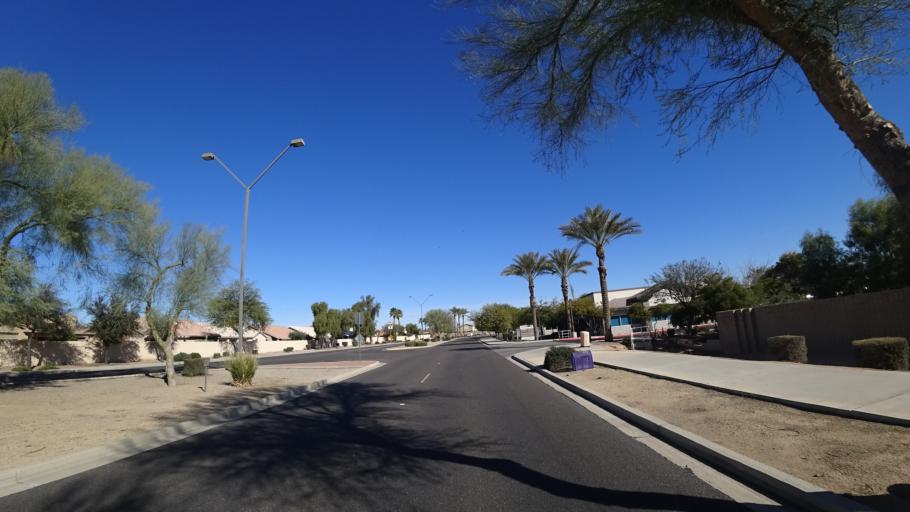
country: US
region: Arizona
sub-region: Maricopa County
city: Litchfield Park
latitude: 33.4848
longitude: -112.3739
